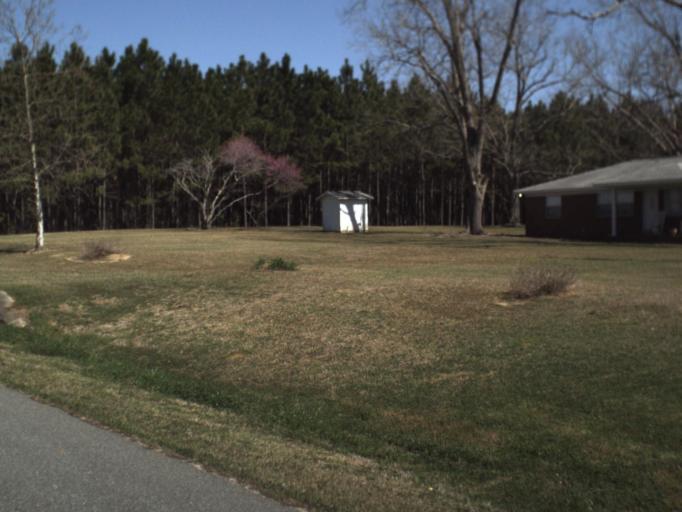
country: US
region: Florida
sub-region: Jackson County
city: Sneads
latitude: 30.6698
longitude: -85.0397
